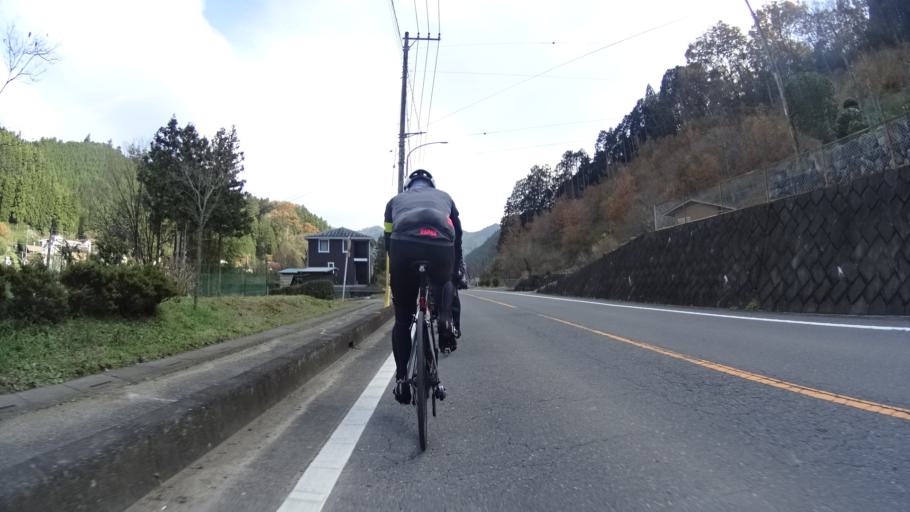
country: JP
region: Tokyo
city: Ome
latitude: 35.8578
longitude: 139.1903
